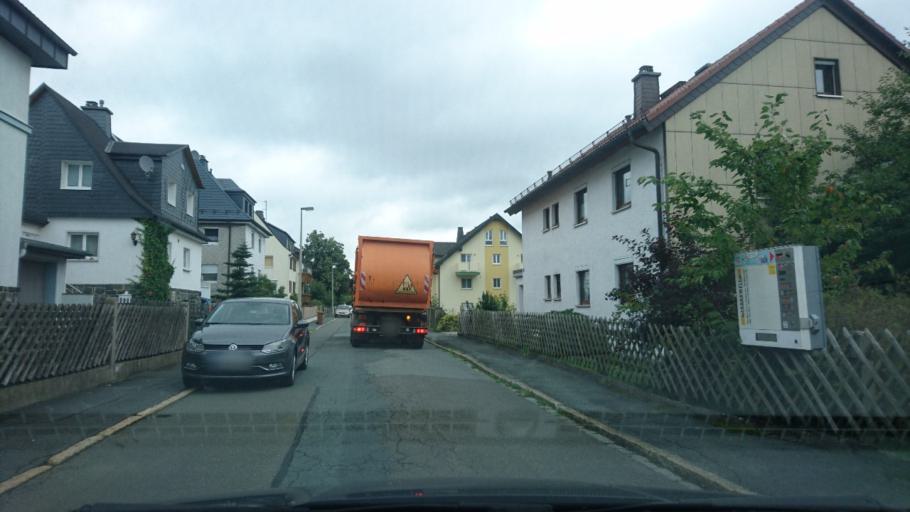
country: DE
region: Bavaria
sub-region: Upper Franconia
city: Naila
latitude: 50.3266
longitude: 11.7016
